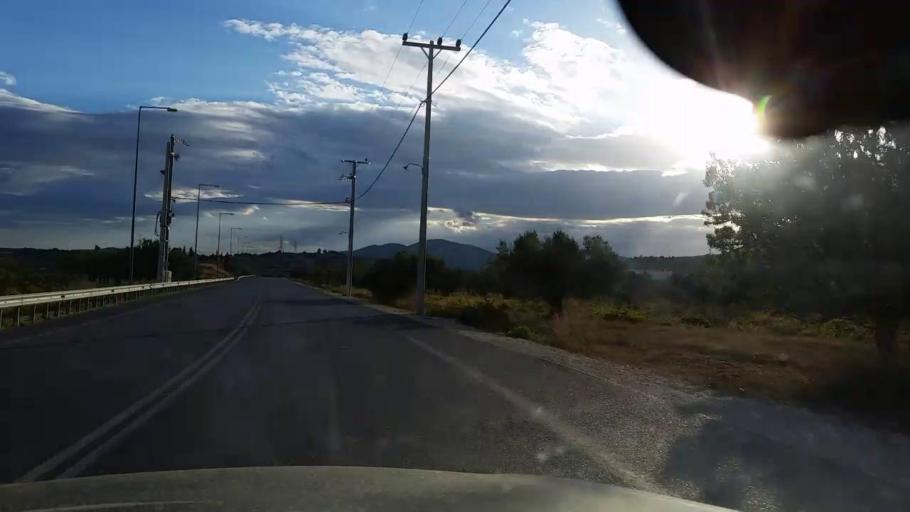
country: GR
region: Attica
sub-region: Nomarchia Anatolikis Attikis
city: Spata
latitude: 37.9622
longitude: 23.8974
